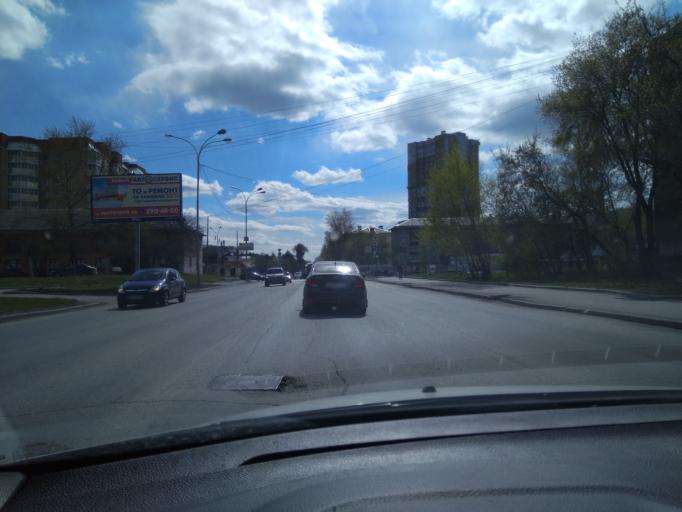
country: RU
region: Sverdlovsk
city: Shuvakish
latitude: 56.8818
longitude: 60.5189
